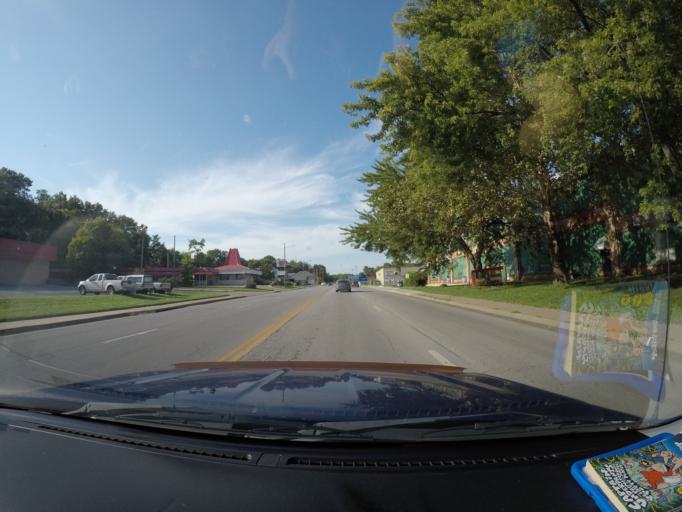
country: US
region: Kansas
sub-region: Leavenworth County
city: Leavenworth
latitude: 39.2984
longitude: -94.9089
